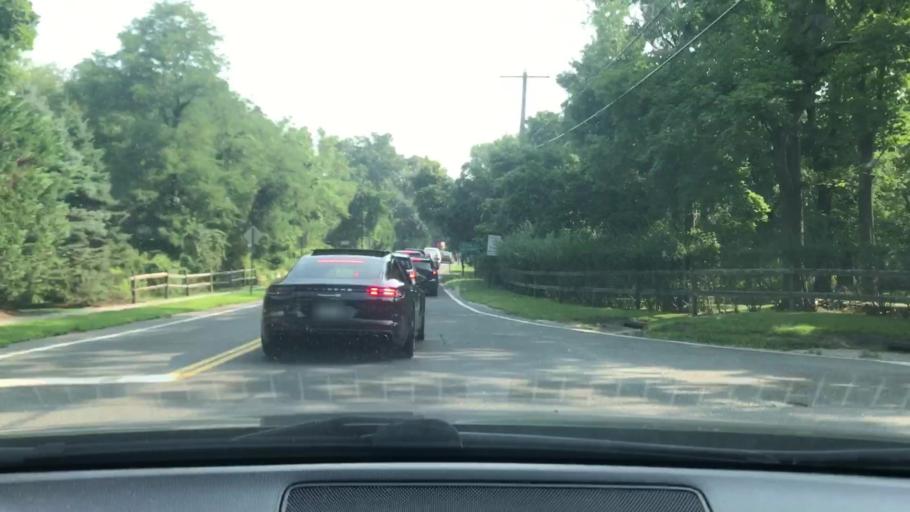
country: US
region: New York
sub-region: Suffolk County
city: Sag Harbor
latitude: 40.9887
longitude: -72.3033
